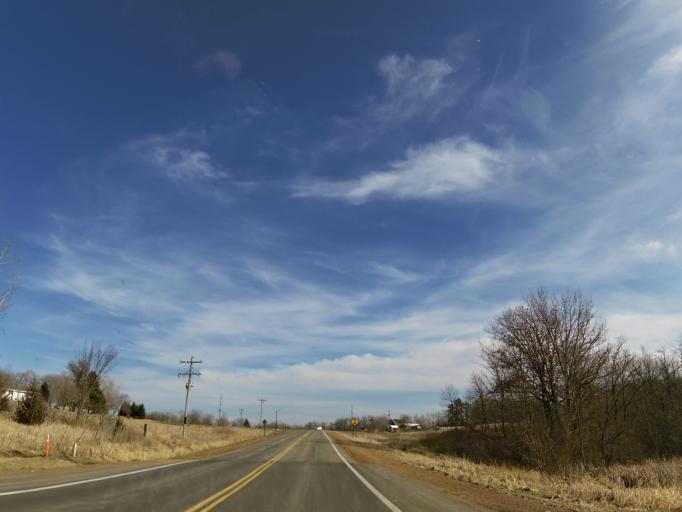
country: US
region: Minnesota
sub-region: Scott County
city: Prior Lake
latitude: 44.6322
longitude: -93.4433
